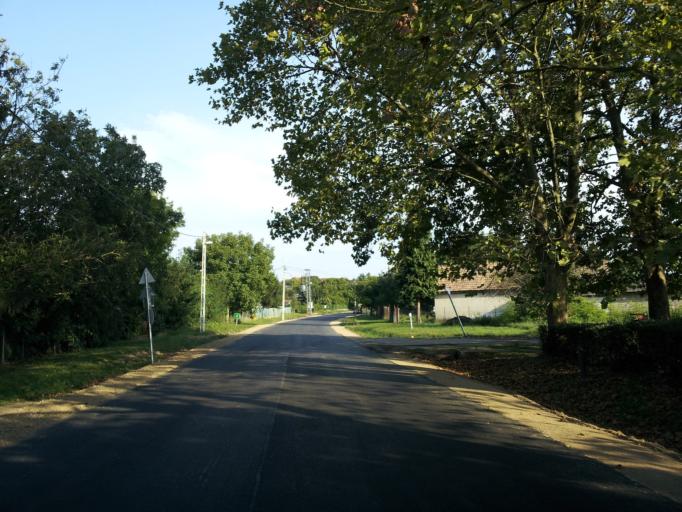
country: HU
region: Somogy
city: Siofok
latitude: 46.8631
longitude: 18.0169
